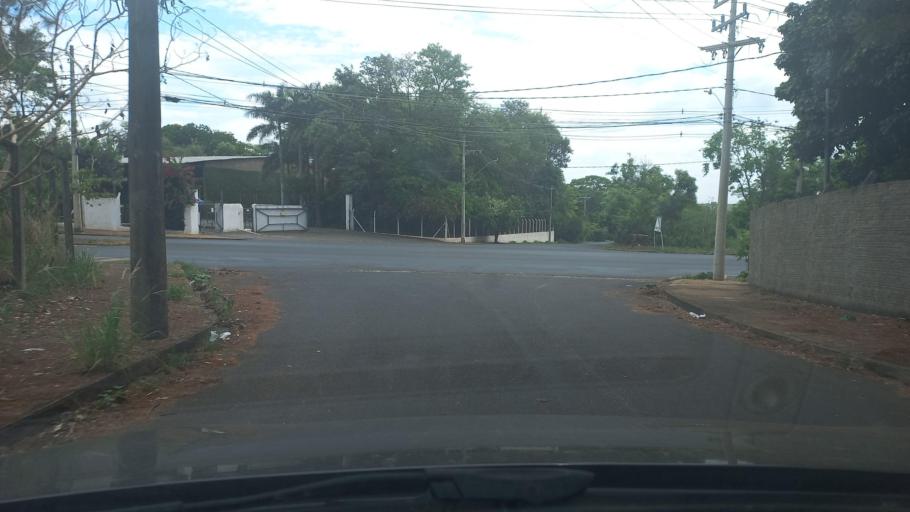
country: BR
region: Minas Gerais
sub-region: Uberaba
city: Uberaba
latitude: -19.7485
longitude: -47.9770
